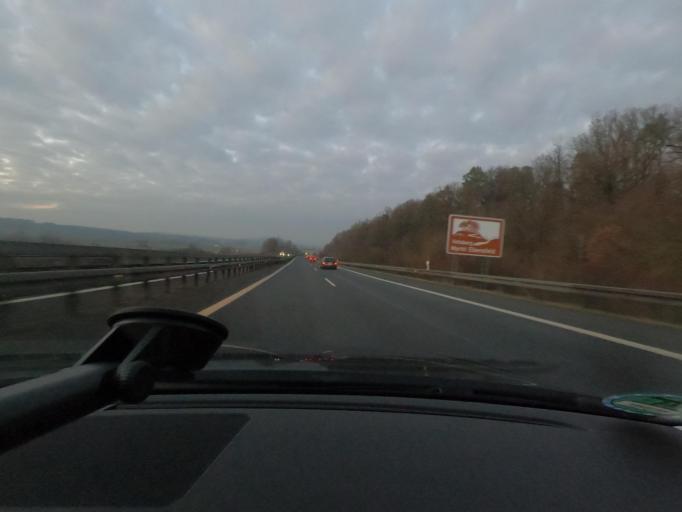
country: DE
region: Bavaria
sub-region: Upper Franconia
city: Ebensfeld
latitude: 50.0411
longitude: 10.9585
